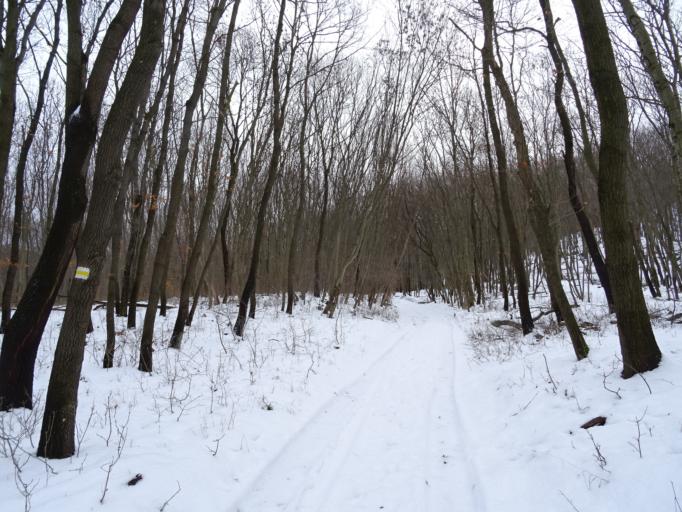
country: HU
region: Komarom-Esztergom
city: Oroszlany
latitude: 47.4692
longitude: 18.3831
